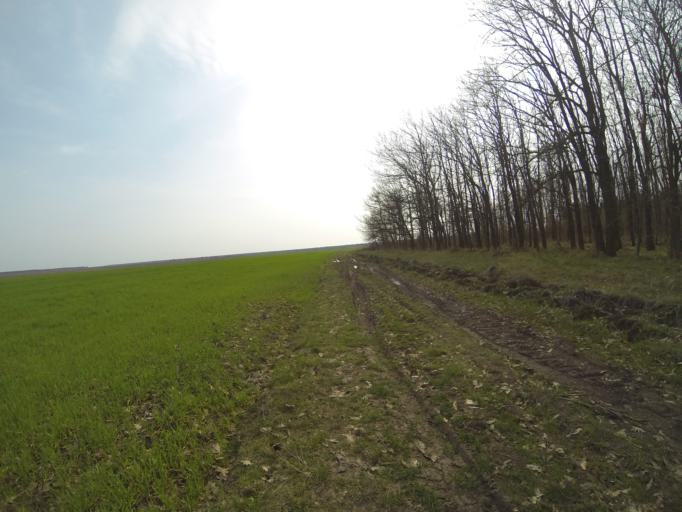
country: RO
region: Dolj
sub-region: Comuna Breasta
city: Breasta
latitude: 44.2721
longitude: 23.6669
